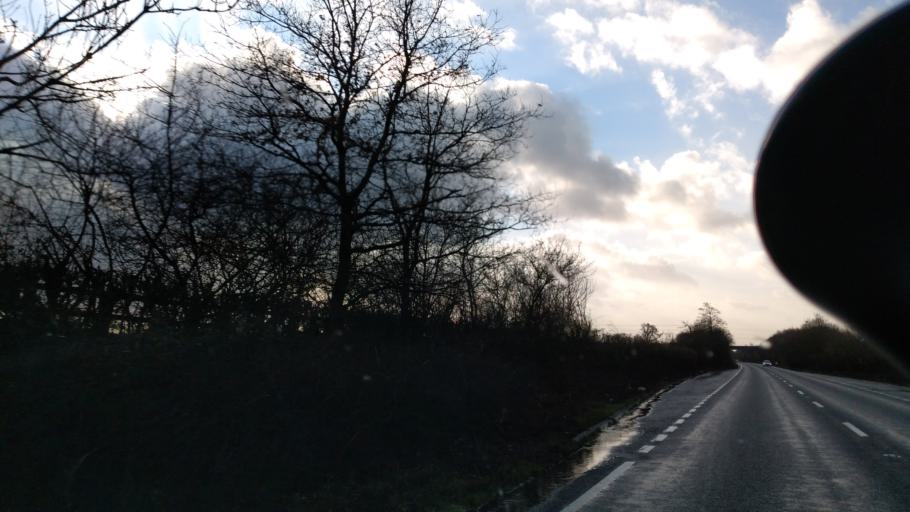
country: GB
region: England
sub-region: Somerset
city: Frome
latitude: 51.2347
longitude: -2.2948
